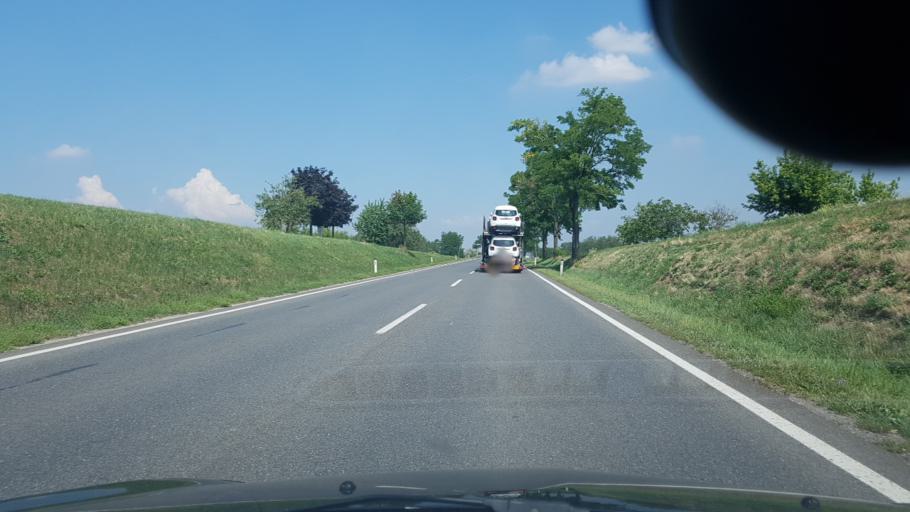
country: AT
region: Lower Austria
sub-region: Politischer Bezirk Mistelbach
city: Drasenhofen
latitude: 48.7644
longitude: 16.6455
